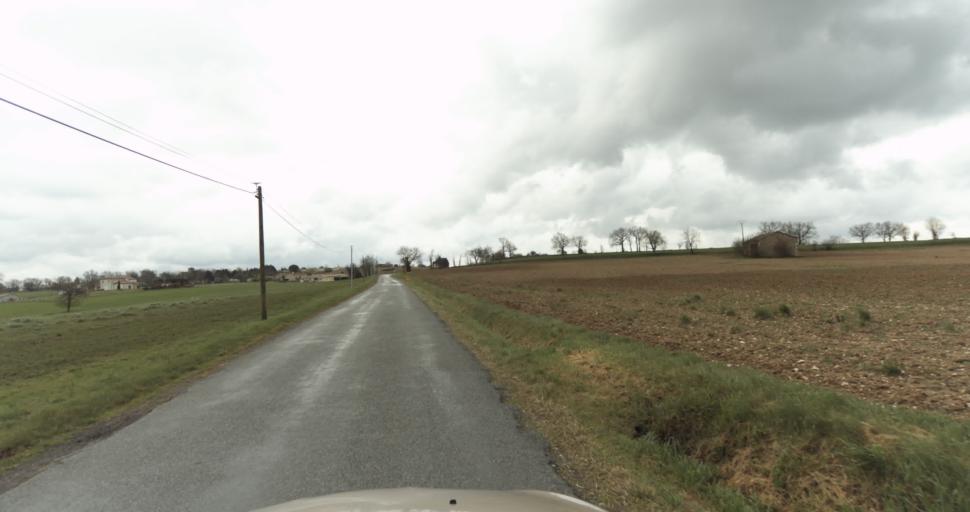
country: FR
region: Midi-Pyrenees
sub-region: Departement du Tarn
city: Frejairolles
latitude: 43.8536
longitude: 2.1967
